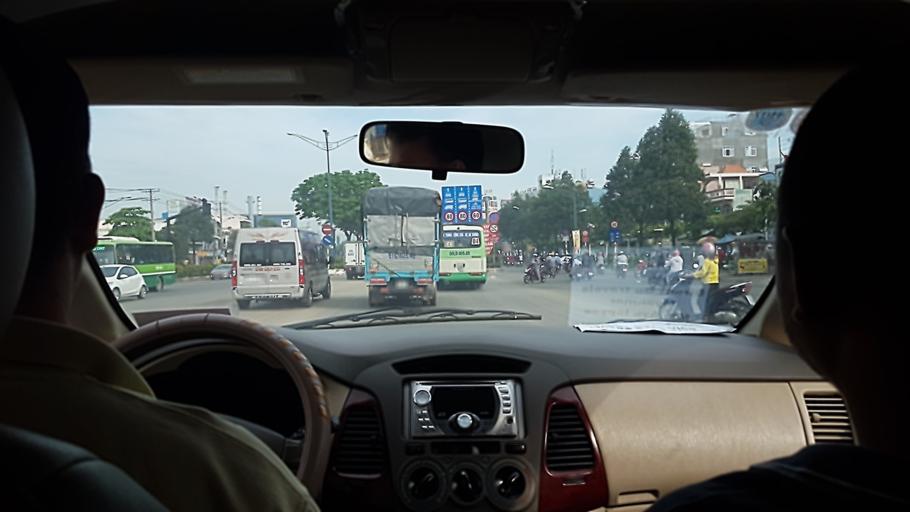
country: VN
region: Ho Chi Minh City
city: Ho Chi Minh City
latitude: 10.8203
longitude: 106.6309
